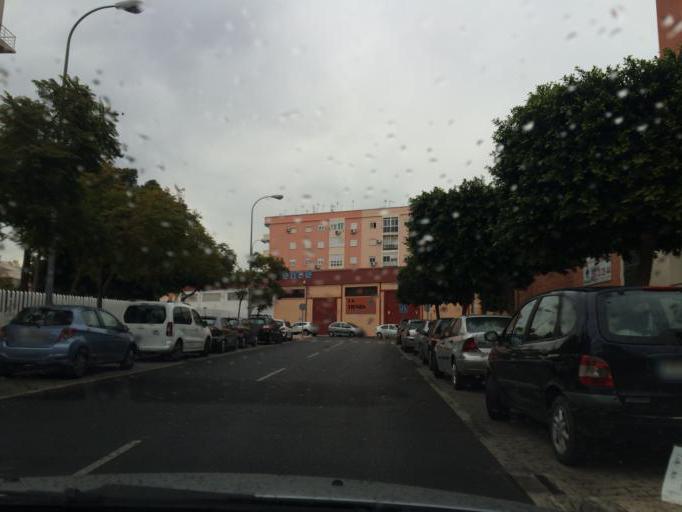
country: ES
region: Andalusia
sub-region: Provincia de Almeria
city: Almeria
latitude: 36.8524
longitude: -2.4509
